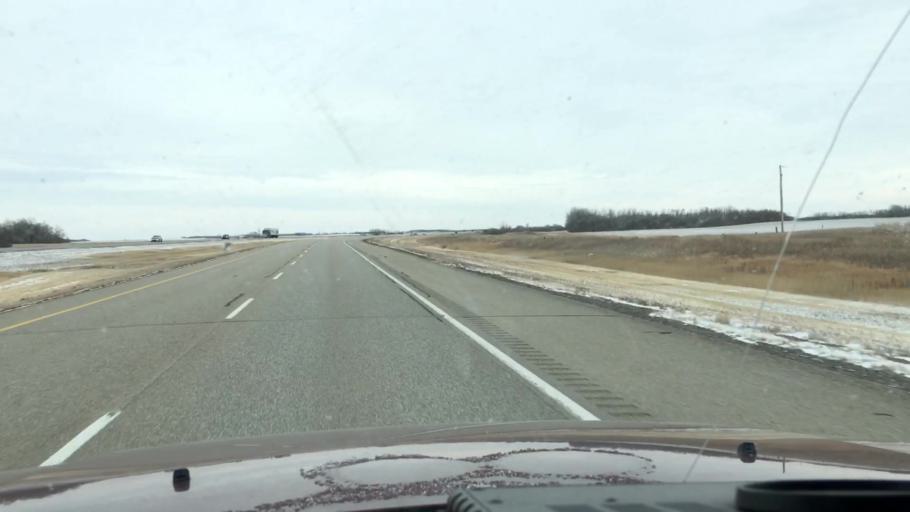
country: CA
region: Saskatchewan
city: Watrous
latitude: 51.3360
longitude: -106.0886
